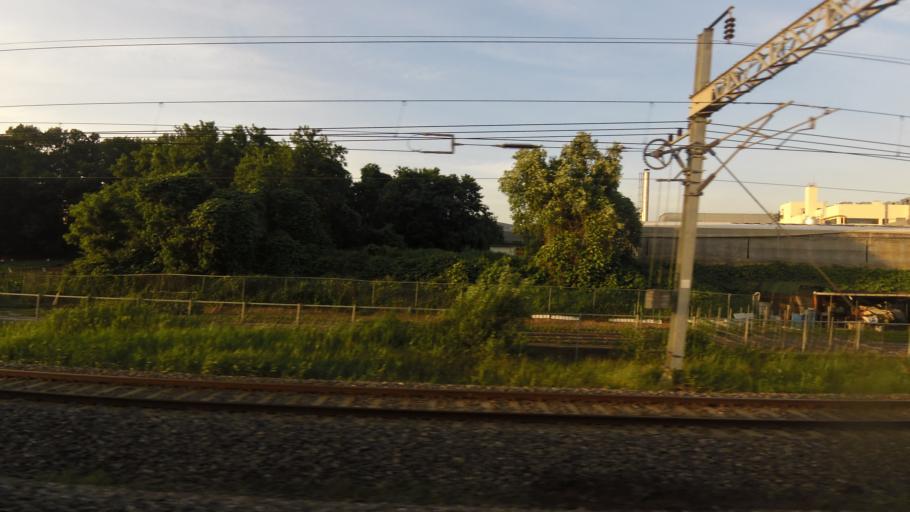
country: KR
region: Gyeonggi-do
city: Osan
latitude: 37.0434
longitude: 127.0591
